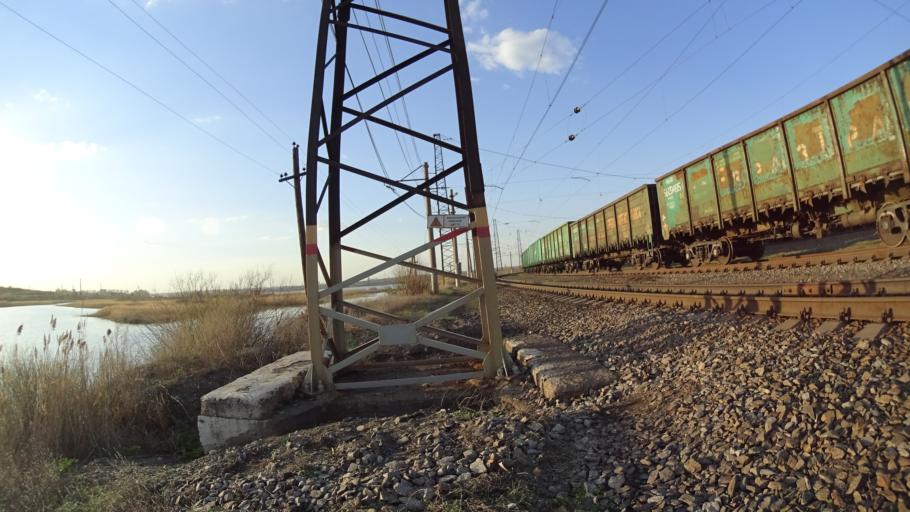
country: RU
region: Chelyabinsk
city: Troitsk
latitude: 54.0528
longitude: 61.6086
